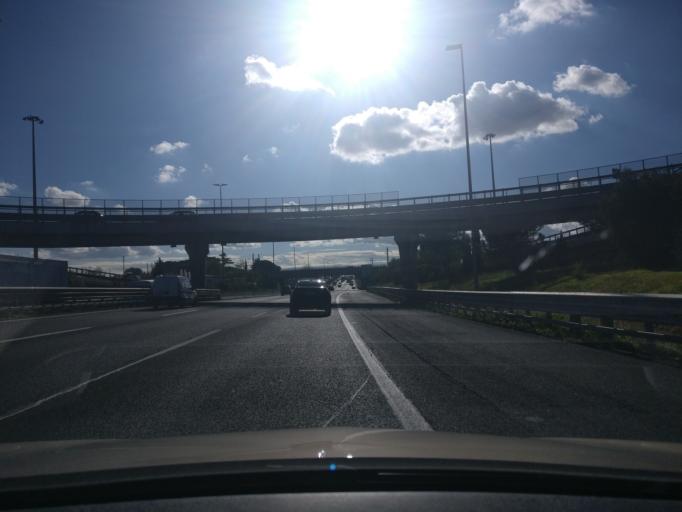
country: IT
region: Latium
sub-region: Citta metropolitana di Roma Capitale
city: Ciampino
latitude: 41.8221
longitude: 12.5800
